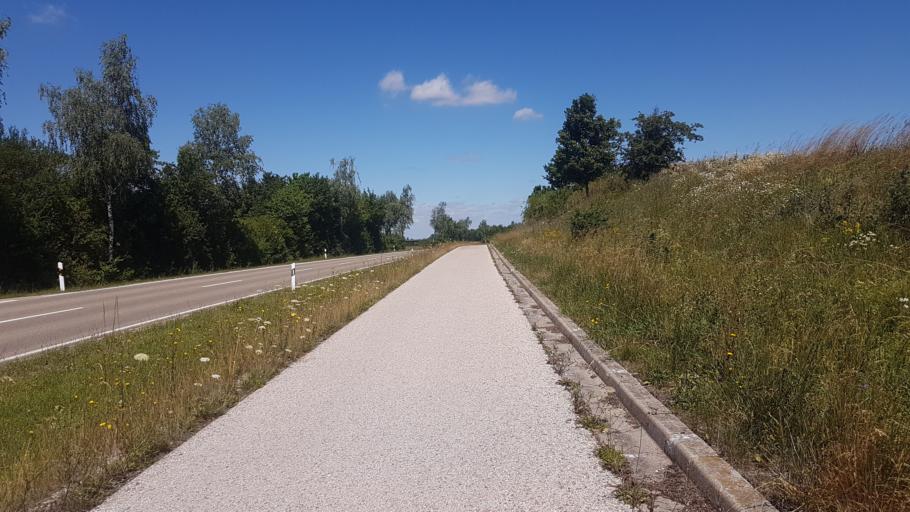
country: DE
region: Bavaria
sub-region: Regierungsbezirk Mittelfranken
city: Herrieden
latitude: 49.2439
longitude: 10.4695
